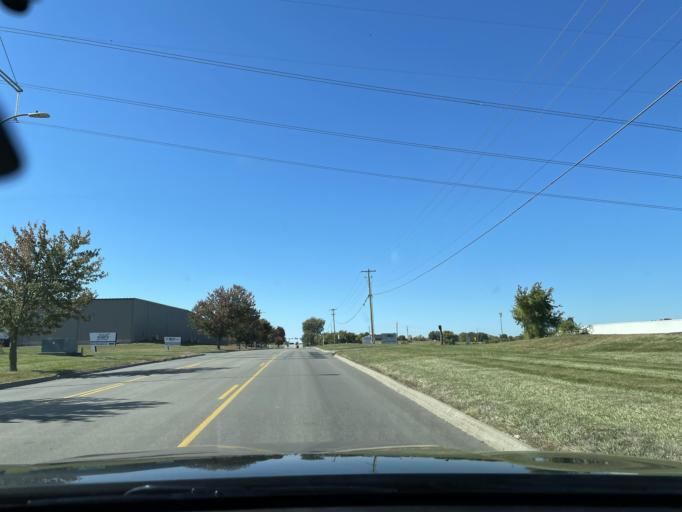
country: US
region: Missouri
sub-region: Buchanan County
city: Saint Joseph
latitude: 39.7555
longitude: -94.7618
